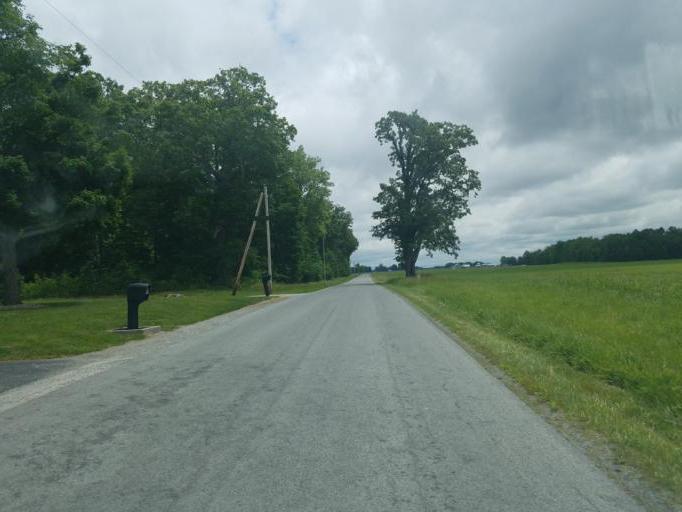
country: US
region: Ohio
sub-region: Crawford County
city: Bucyrus
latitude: 40.7757
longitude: -83.0410
